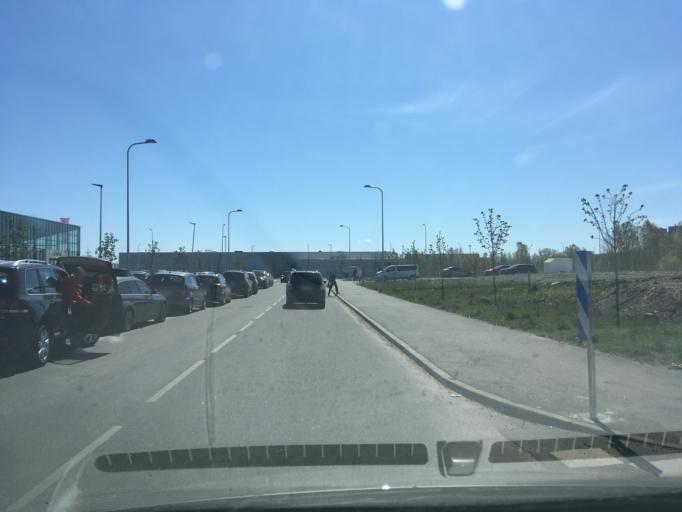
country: EE
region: Harju
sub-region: Tallinna linn
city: Kose
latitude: 59.4428
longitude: 24.8515
